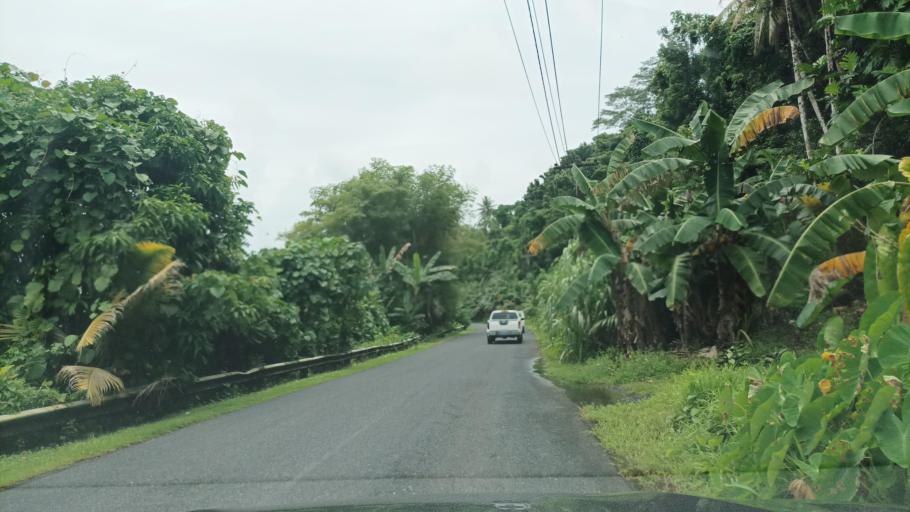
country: FM
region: Pohnpei
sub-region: Kolonia Municipality
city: Kolonia Town
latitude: 6.9515
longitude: 158.1933
